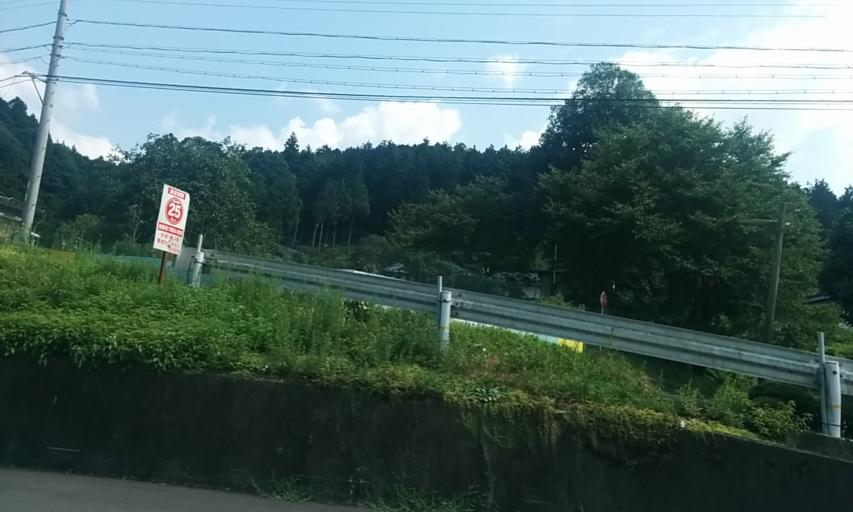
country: JP
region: Kyoto
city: Fukuchiyama
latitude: 35.3648
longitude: 135.1211
